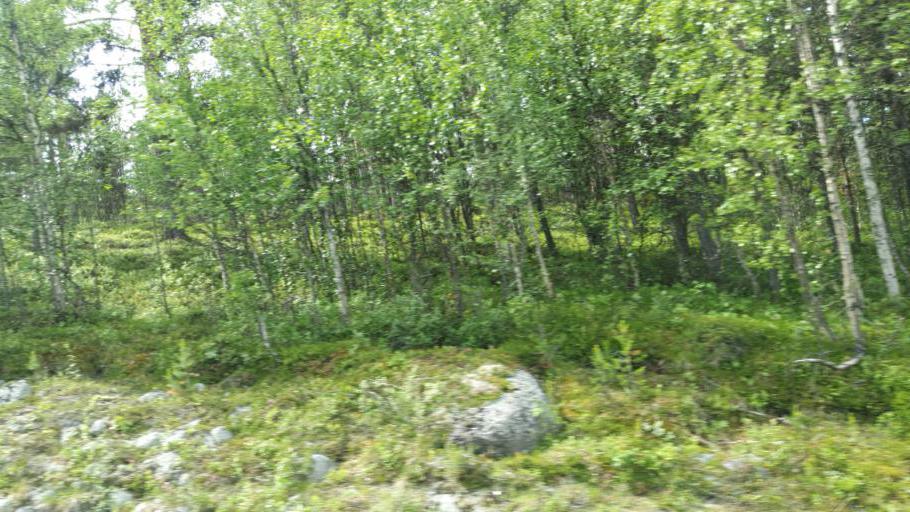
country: NO
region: Oppland
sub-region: Vaga
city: Vagamo
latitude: 61.7093
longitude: 9.0568
